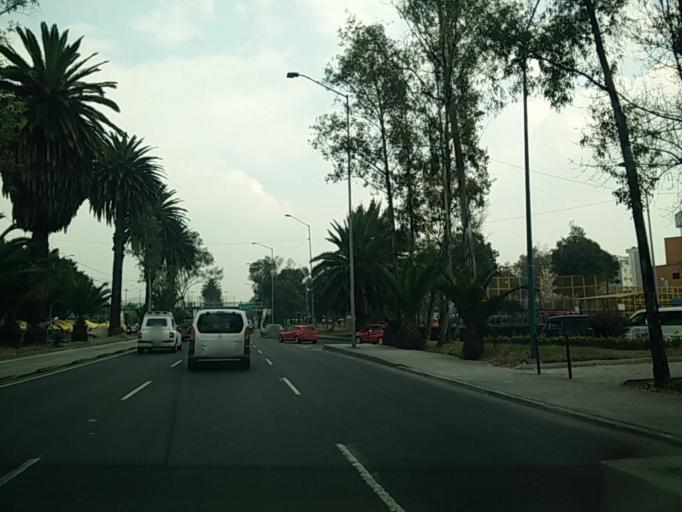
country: MX
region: Mexico City
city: Cuauhtemoc
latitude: 19.4674
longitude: -99.1400
